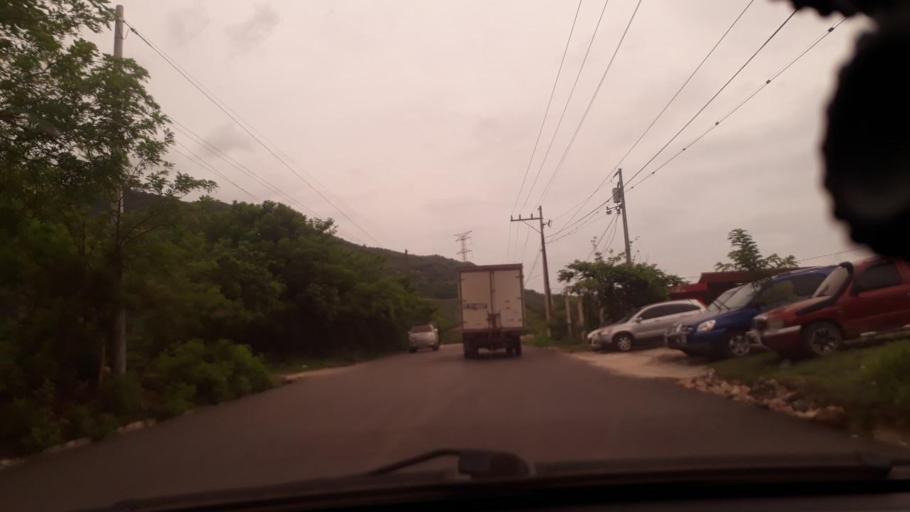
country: GT
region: Chiquimula
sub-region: Municipio de San Juan Ermita
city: San Juan Ermita
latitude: 14.7587
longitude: -89.4392
